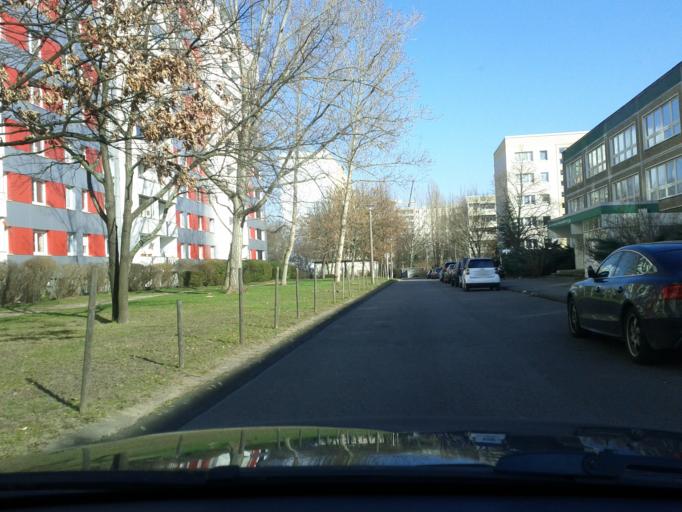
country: DE
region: Berlin
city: Friedrichsfelde
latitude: 52.5131
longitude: 13.5277
